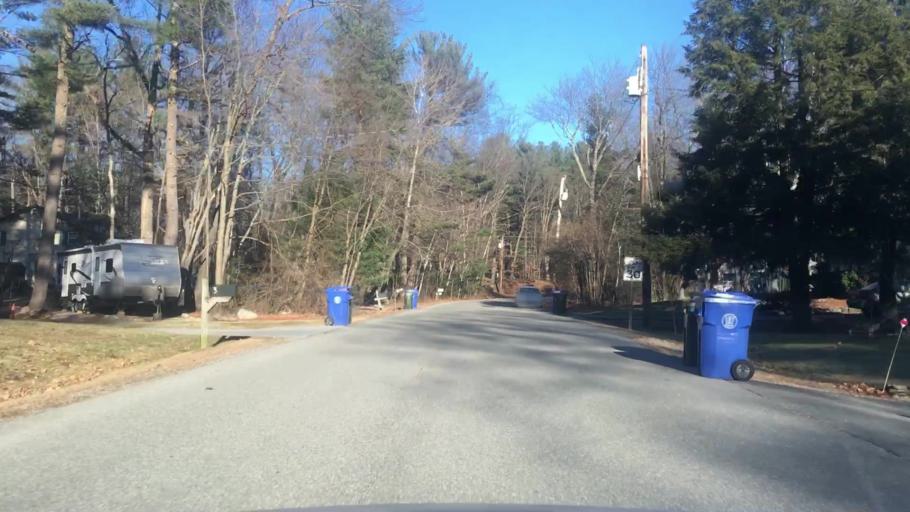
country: US
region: New Hampshire
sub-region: Rockingham County
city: Londonderry
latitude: 42.8822
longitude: -71.3666
